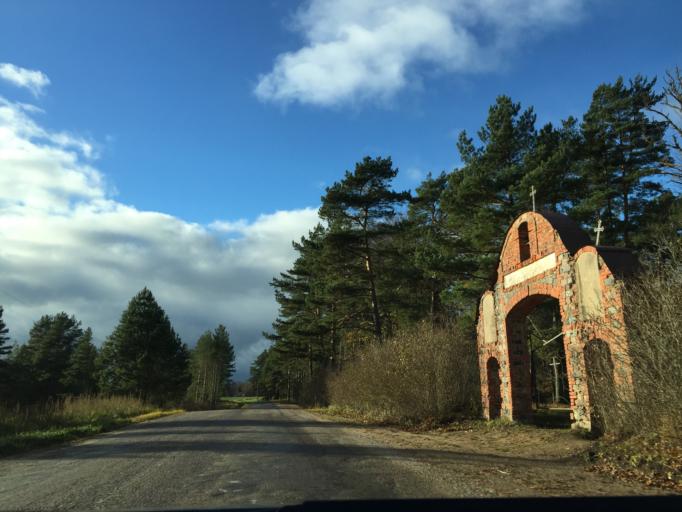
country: LV
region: Kandava
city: Kandava
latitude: 56.9692
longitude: 22.9413
